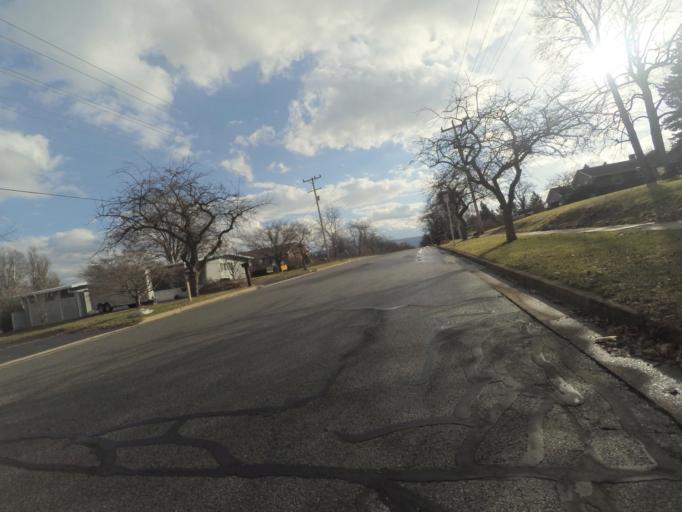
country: US
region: Pennsylvania
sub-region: Centre County
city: State College
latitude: 40.7928
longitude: -77.8380
